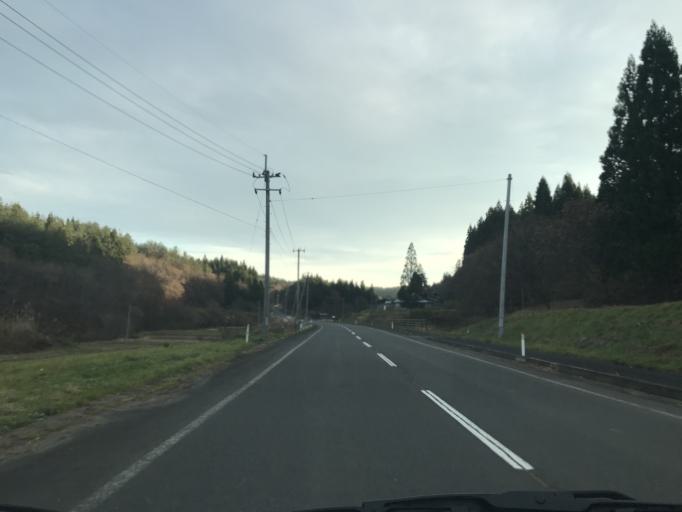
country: JP
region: Iwate
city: Ichinoseki
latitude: 38.9920
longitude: 141.0661
